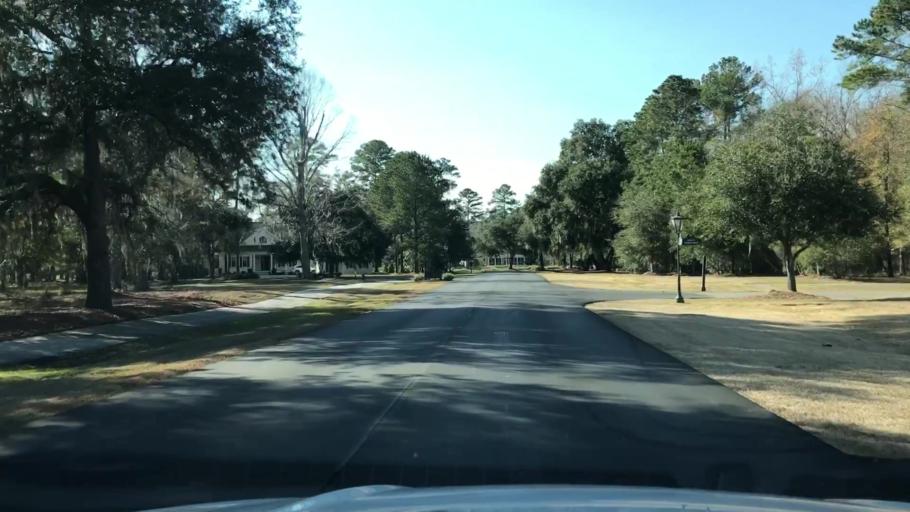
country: US
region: South Carolina
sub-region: Beaufort County
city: Bluffton
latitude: 32.3418
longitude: -80.9157
